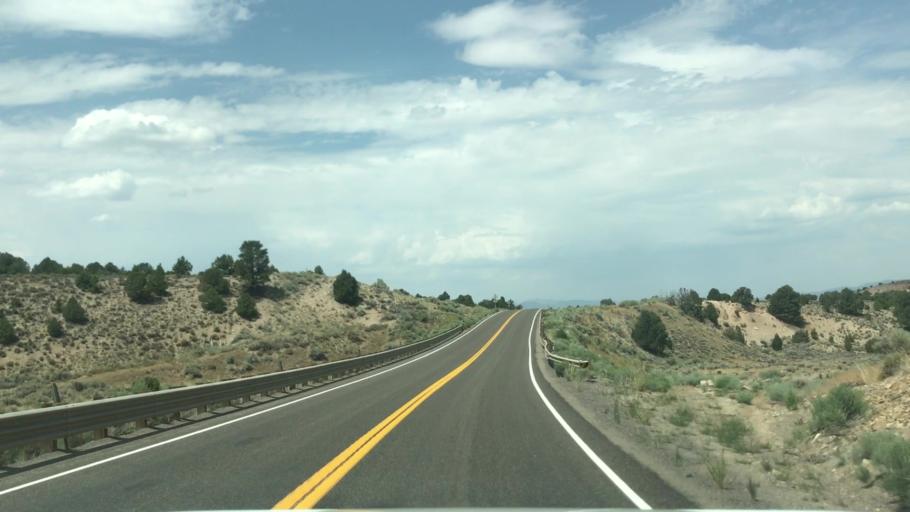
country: US
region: Nevada
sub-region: Eureka County
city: Eureka
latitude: 39.3911
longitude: -115.5024
